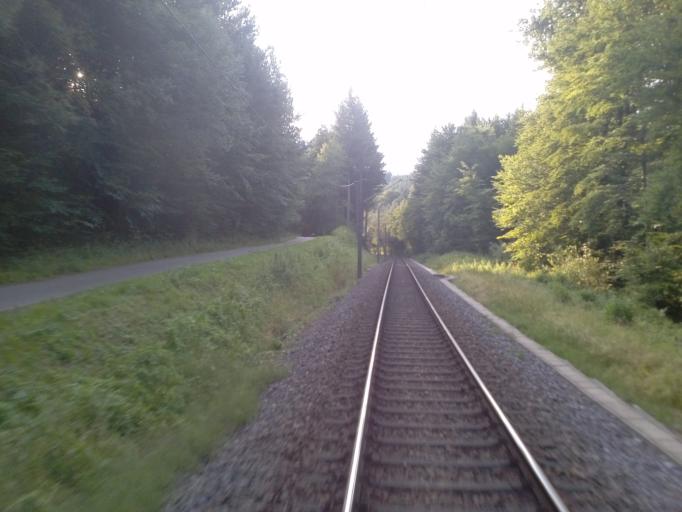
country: DE
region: Baden-Wuerttemberg
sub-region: Karlsruhe Region
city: Ettlingen
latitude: 48.9227
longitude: 8.4661
